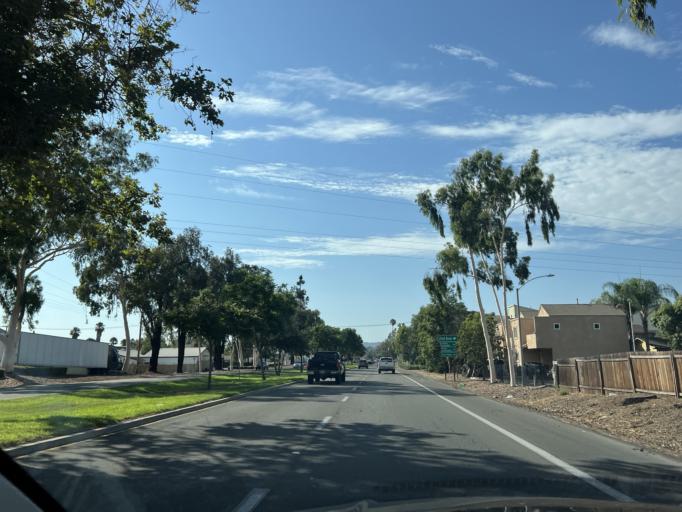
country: US
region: California
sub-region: San Diego County
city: Escondido
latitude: 33.1161
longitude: -117.0845
